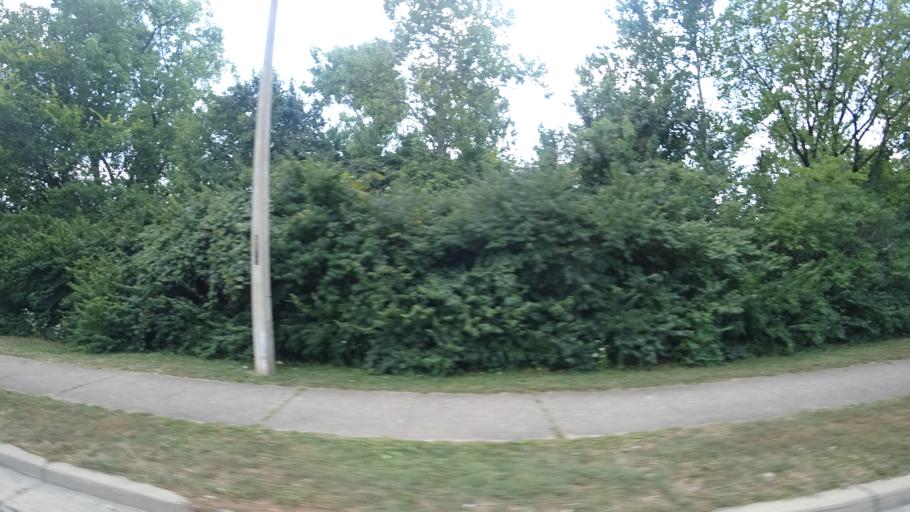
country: US
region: Ohio
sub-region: Butler County
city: Hamilton
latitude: 39.4226
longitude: -84.5810
